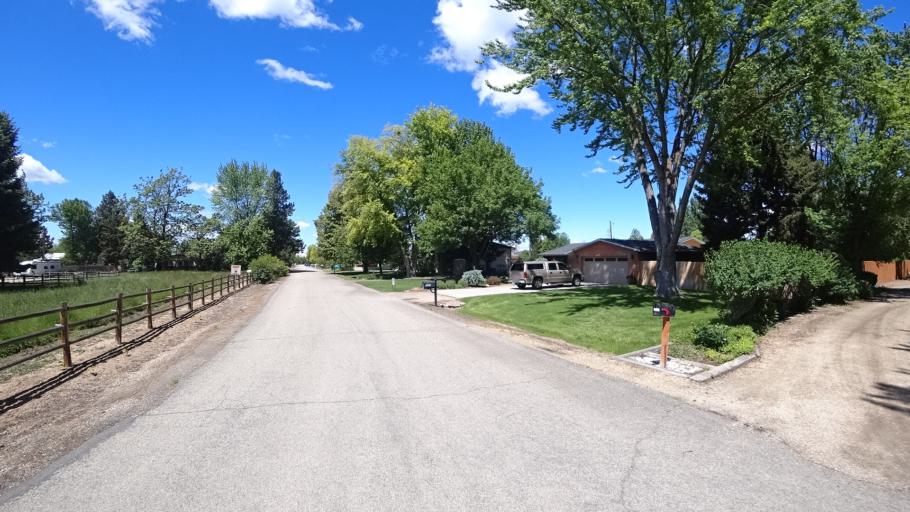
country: US
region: Idaho
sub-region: Ada County
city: Meridian
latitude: 43.6257
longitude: -116.3405
